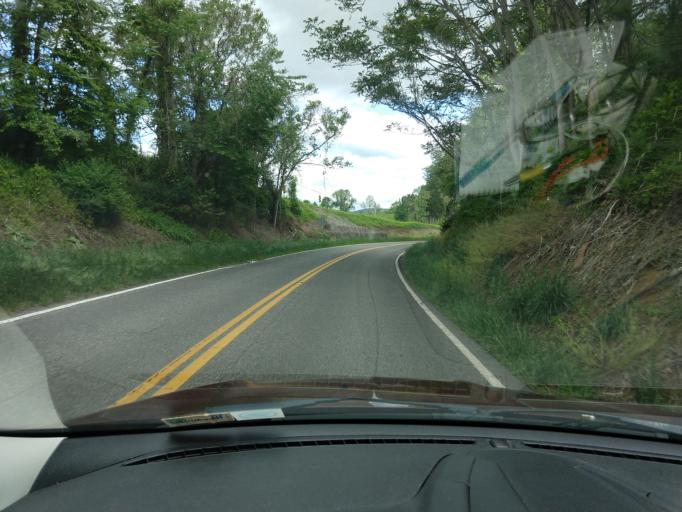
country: US
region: Virginia
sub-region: Wythe County
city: Wytheville
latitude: 36.8437
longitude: -80.9710
